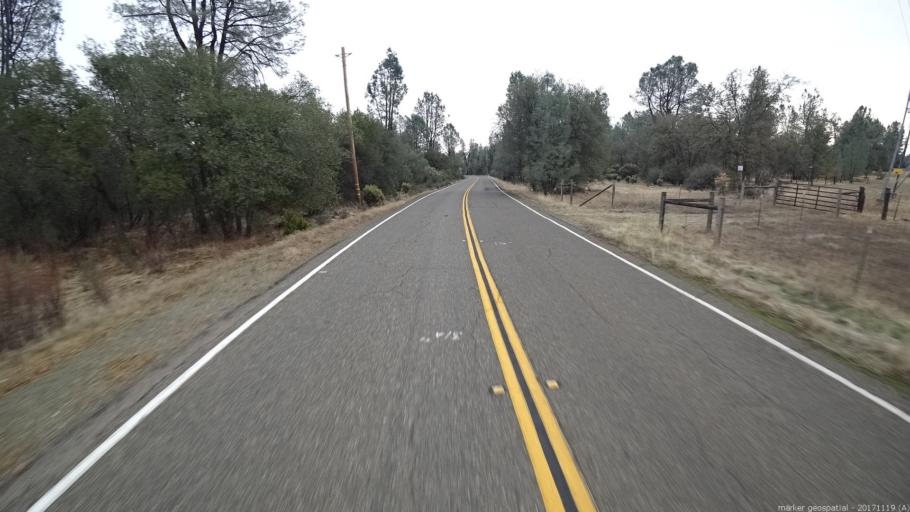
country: US
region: California
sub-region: Shasta County
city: Redding
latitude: 40.4881
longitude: -122.4266
